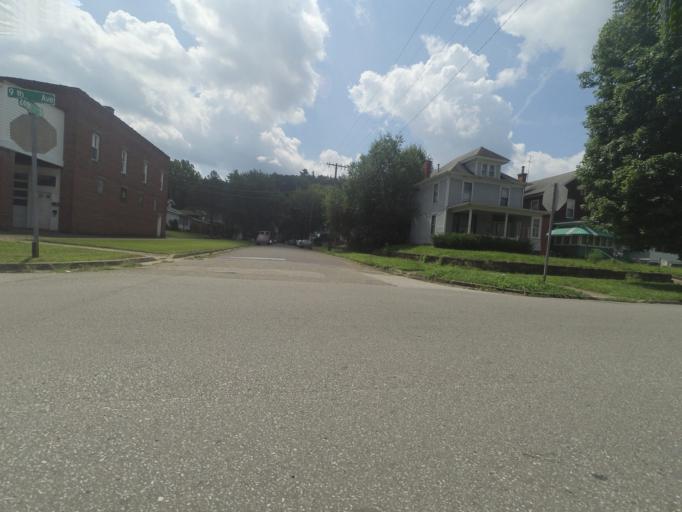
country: US
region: West Virginia
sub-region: Cabell County
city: Huntington
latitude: 38.4186
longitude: -82.4141
